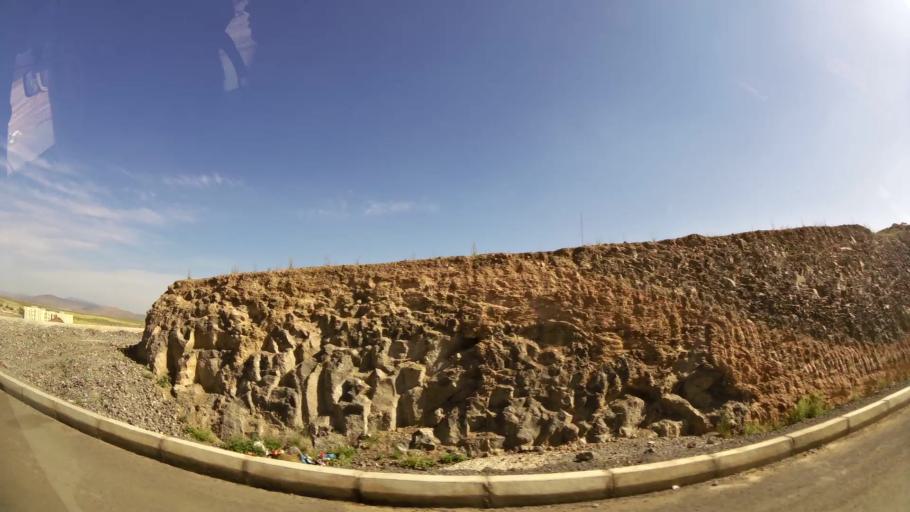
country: MA
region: Oriental
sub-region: Oujda-Angad
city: Oujda
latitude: 34.6479
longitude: -1.9512
